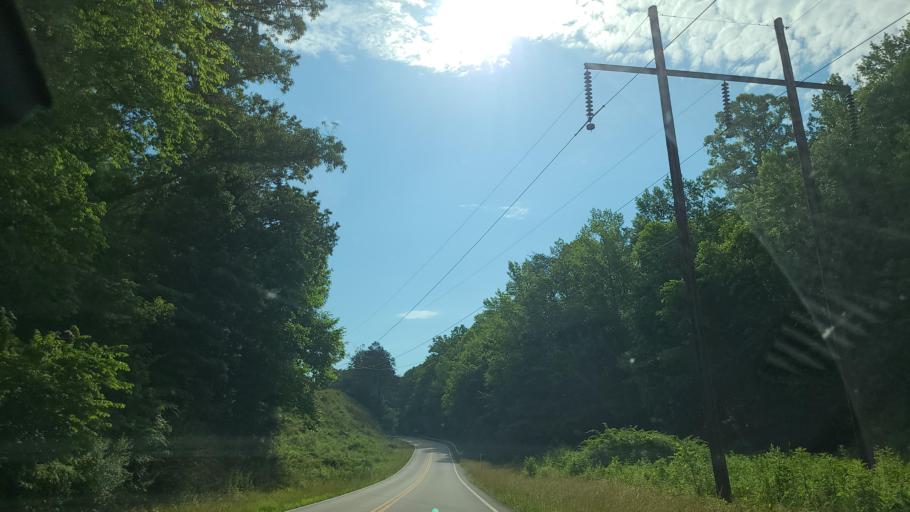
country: US
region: Kentucky
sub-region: Knox County
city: Barbourville
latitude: 36.6854
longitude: -83.8863
